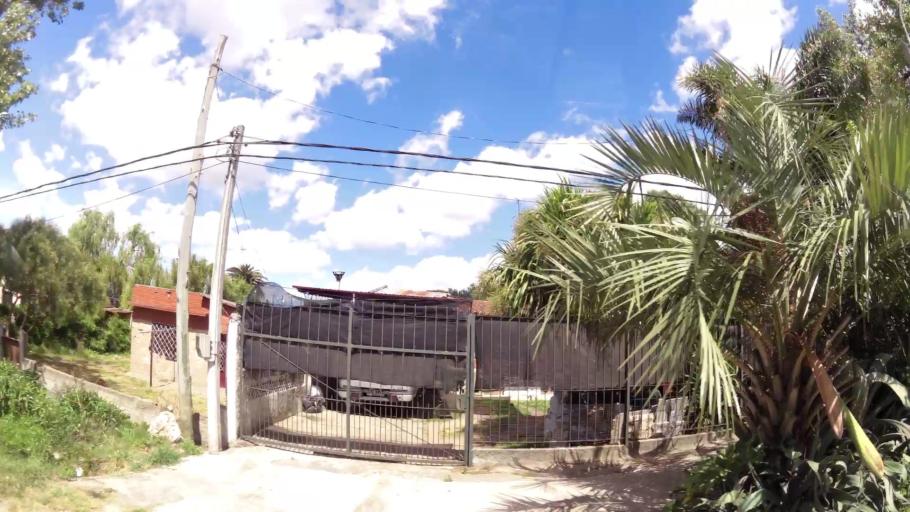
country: UY
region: Canelones
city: Paso de Carrasco
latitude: -34.8280
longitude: -56.1127
